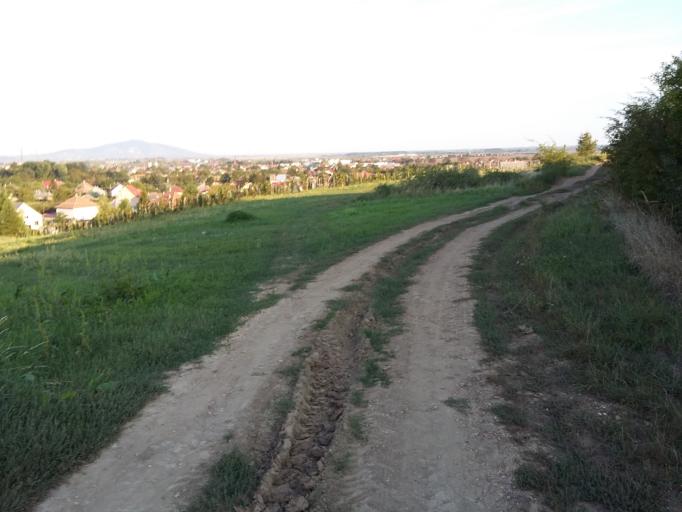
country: HU
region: Borsod-Abauj-Zemplen
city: Bekecs
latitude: 48.1609
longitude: 21.1763
